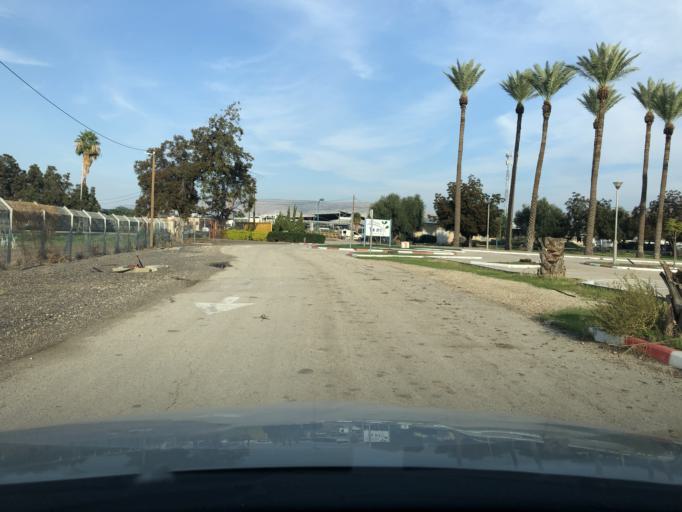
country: IL
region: Northern District
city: Yavne'el
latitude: 32.6639
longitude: 35.5806
